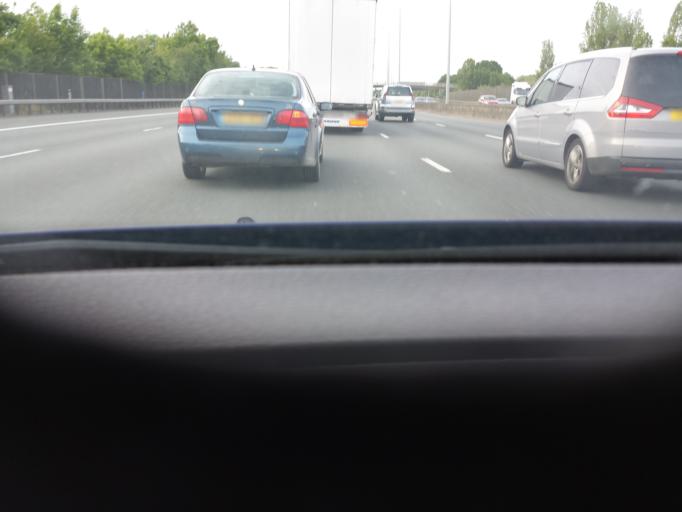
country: GB
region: England
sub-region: Surrey
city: Egham
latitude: 51.4113
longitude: -0.5411
